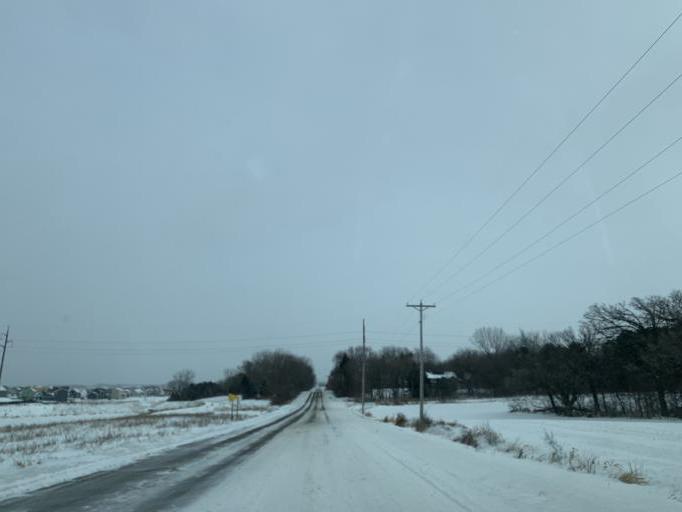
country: US
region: Minnesota
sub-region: Washington County
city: Cottage Grove
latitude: 44.8763
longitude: -92.9357
